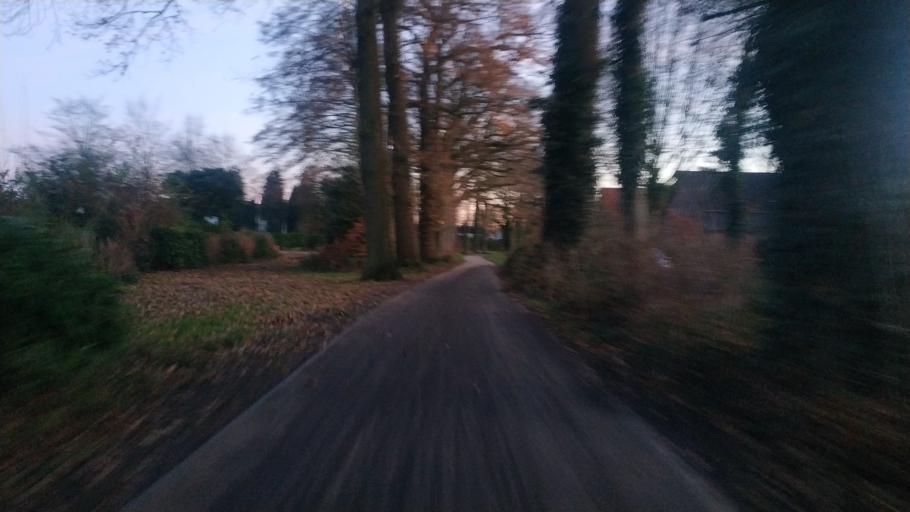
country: DE
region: North Rhine-Westphalia
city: Ibbenburen
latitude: 52.2723
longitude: 7.6987
